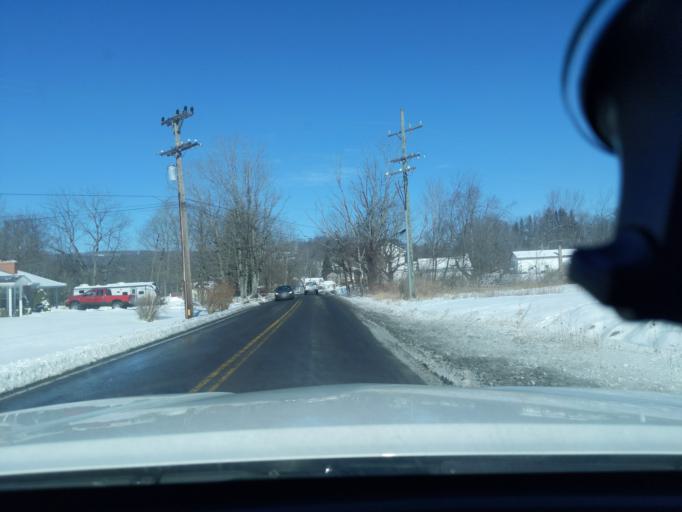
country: US
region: Maryland
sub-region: Allegany County
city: Frostburg
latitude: 39.6370
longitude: -78.9287
